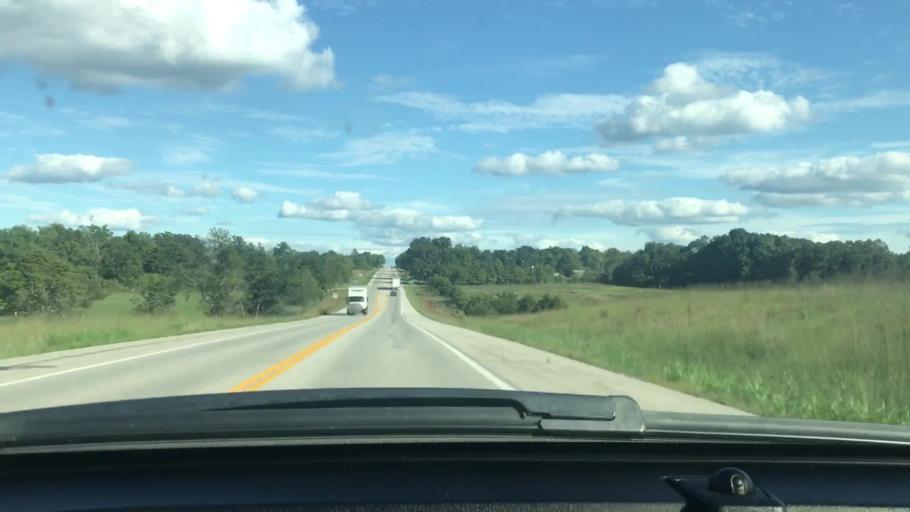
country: US
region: Missouri
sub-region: Howell County
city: West Plains
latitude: 36.6559
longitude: -91.6990
